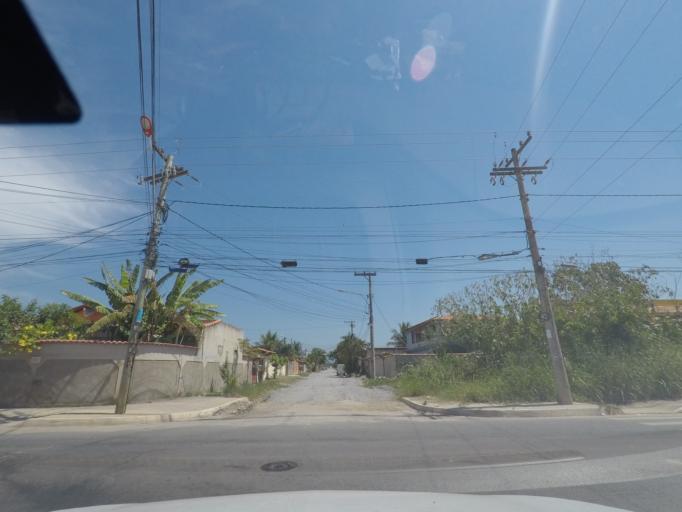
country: BR
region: Rio de Janeiro
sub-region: Marica
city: Marica
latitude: -22.9566
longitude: -42.9568
